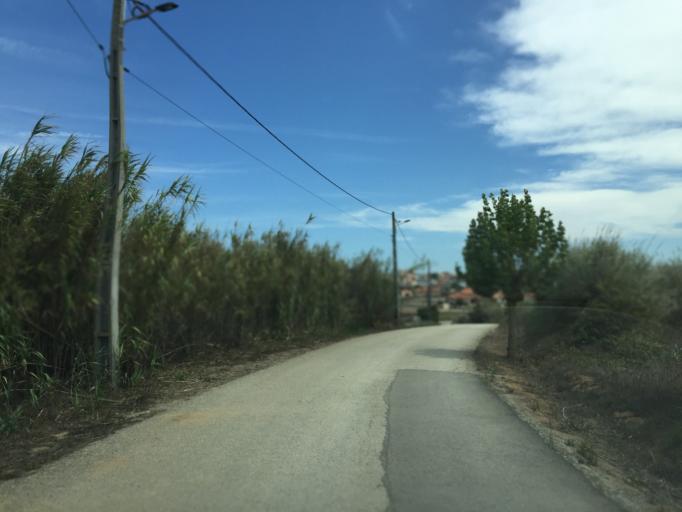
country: PT
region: Lisbon
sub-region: Lourinha
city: Lourinha
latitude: 39.2059
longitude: -9.3400
